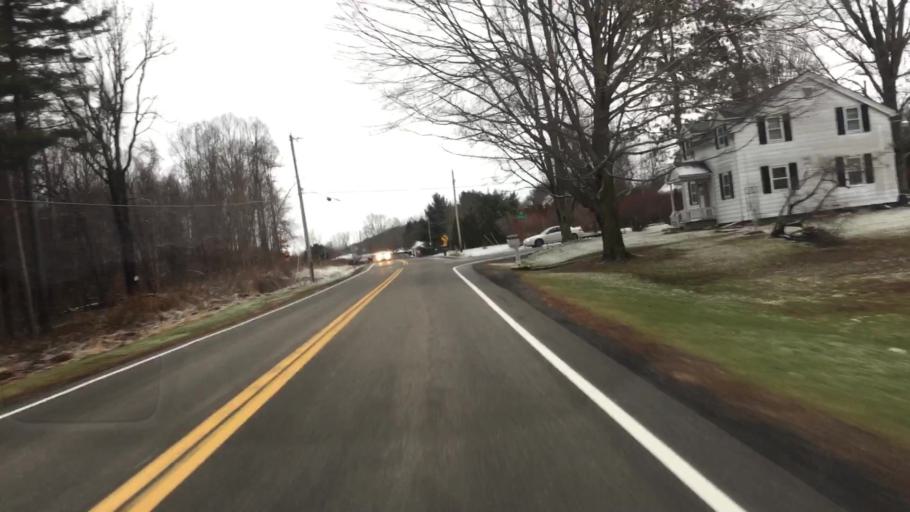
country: US
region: Ohio
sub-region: Summit County
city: Norton
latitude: 41.0690
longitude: -81.6260
